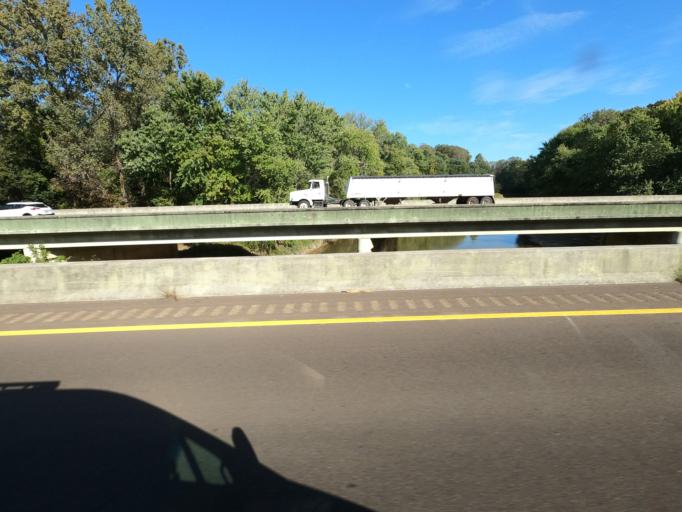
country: US
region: Tennessee
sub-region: Obion County
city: Obion
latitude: 36.2403
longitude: -89.2176
